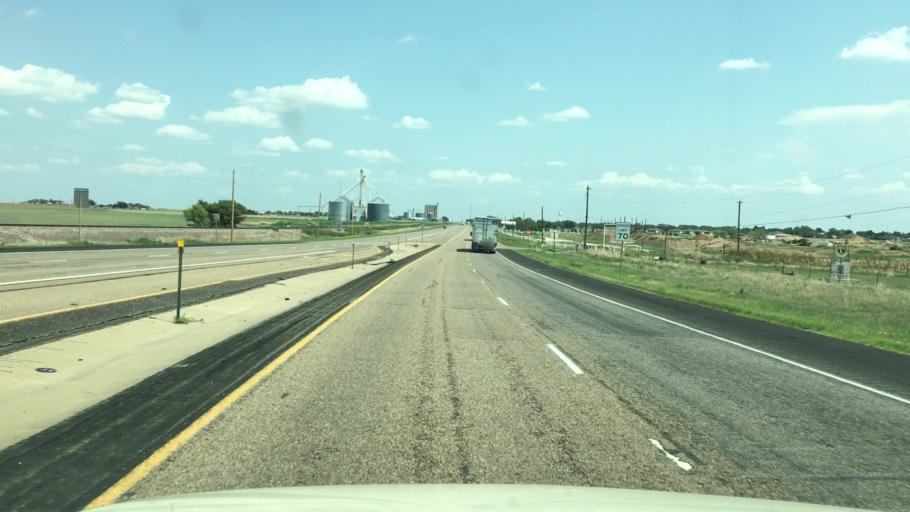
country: US
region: Texas
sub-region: Armstrong County
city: Claude
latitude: 35.1199
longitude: -101.3825
